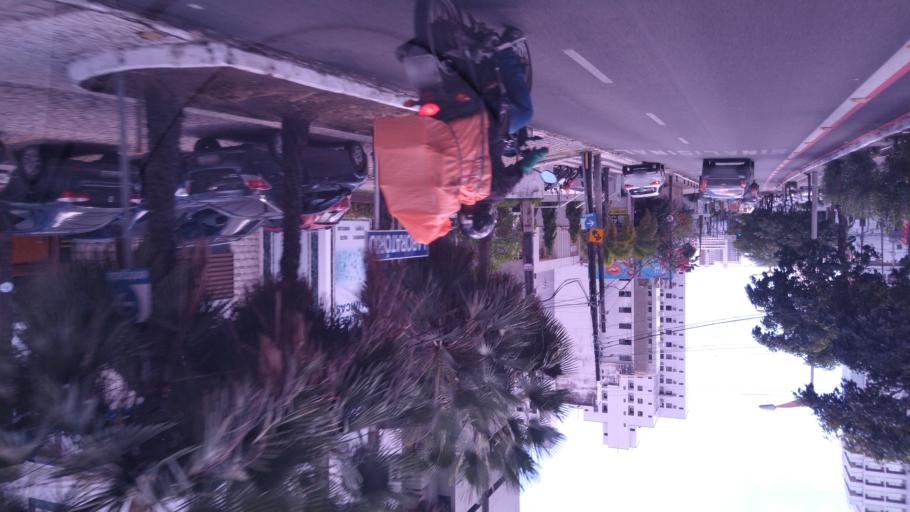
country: BR
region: Ceara
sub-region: Fortaleza
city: Fortaleza
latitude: -3.7406
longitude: -38.4943
